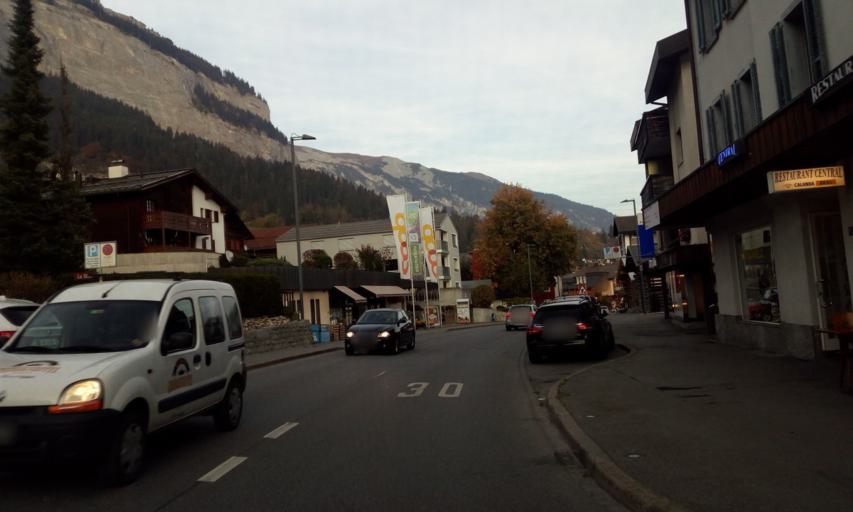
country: CH
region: Grisons
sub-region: Imboden District
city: Flims
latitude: 46.8366
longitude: 9.2847
